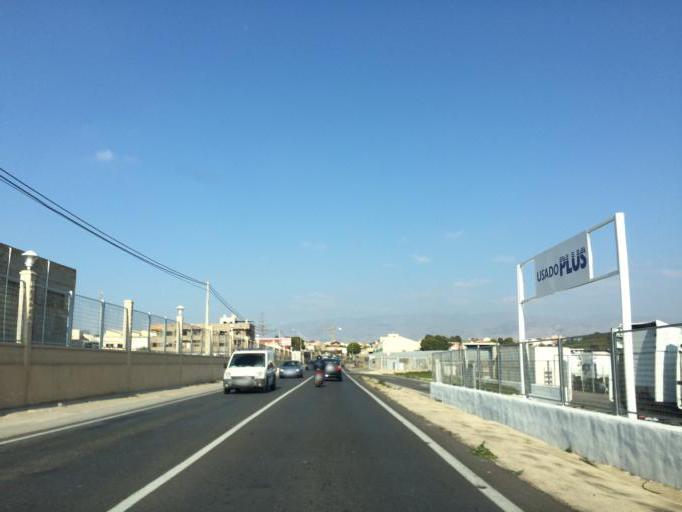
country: ES
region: Andalusia
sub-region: Provincia de Almeria
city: Huercal de Almeria
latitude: 36.8597
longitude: -2.4196
